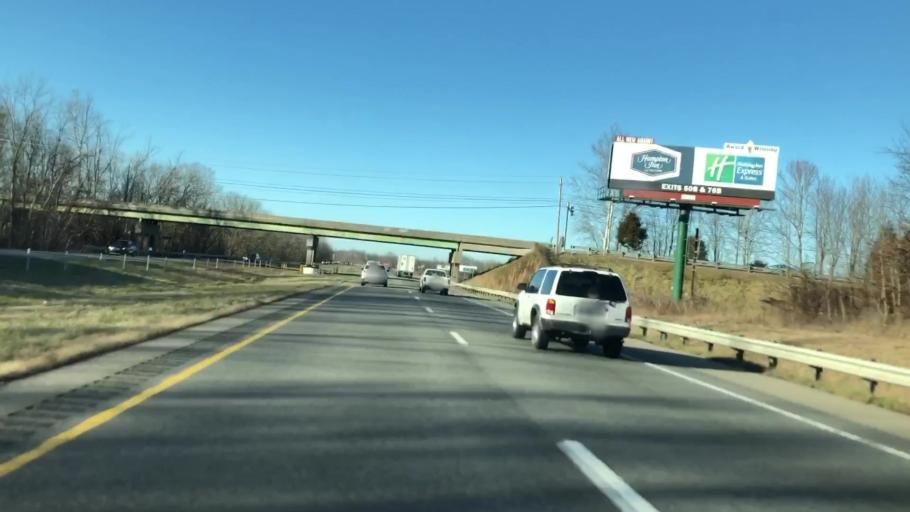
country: US
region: Indiana
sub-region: Scott County
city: Scottsburg
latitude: 38.7064
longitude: -85.7939
